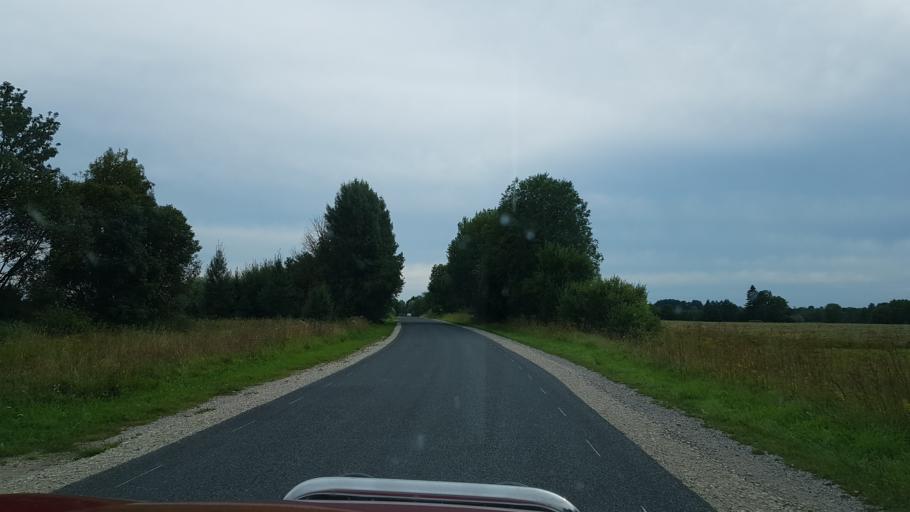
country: EE
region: Laeaene
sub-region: Lihula vald
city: Lihula
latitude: 58.8813
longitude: 23.8562
